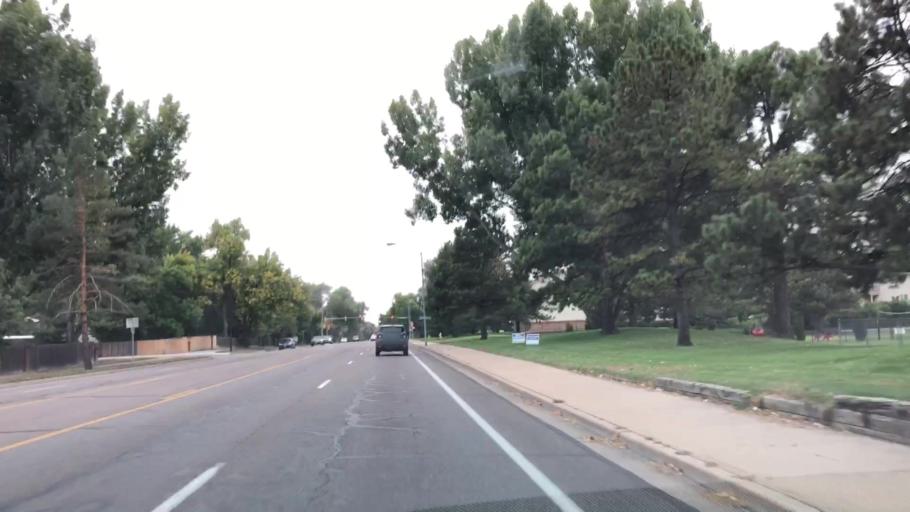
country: US
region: Colorado
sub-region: Larimer County
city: Fort Collins
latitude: 40.5477
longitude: -105.0581
